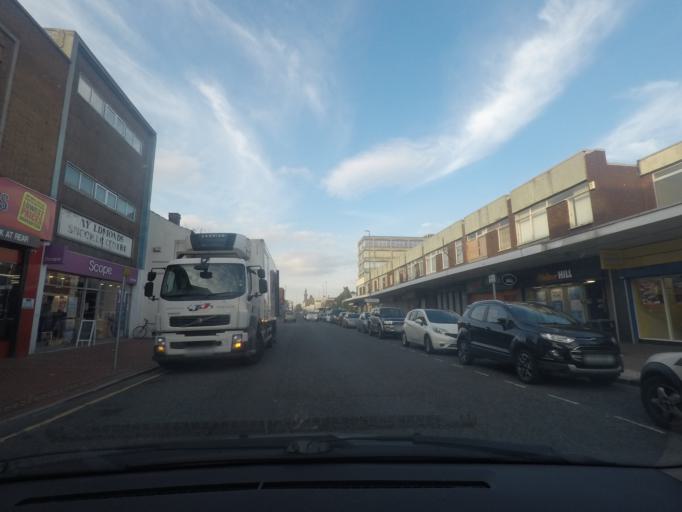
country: GB
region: England
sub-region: North East Lincolnshire
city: Grimsby
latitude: 53.5722
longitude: -0.0734
